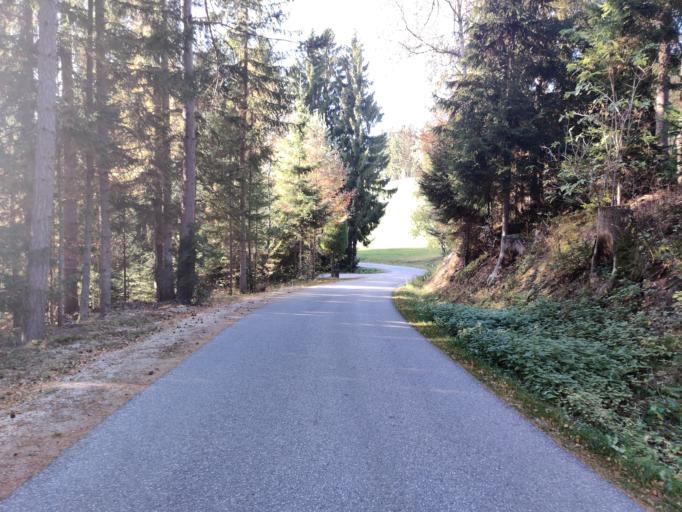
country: AT
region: Styria
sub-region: Politischer Bezirk Hartberg-Fuerstenfeld
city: Sankt Jakob im Walde
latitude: 47.4680
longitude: 15.8043
